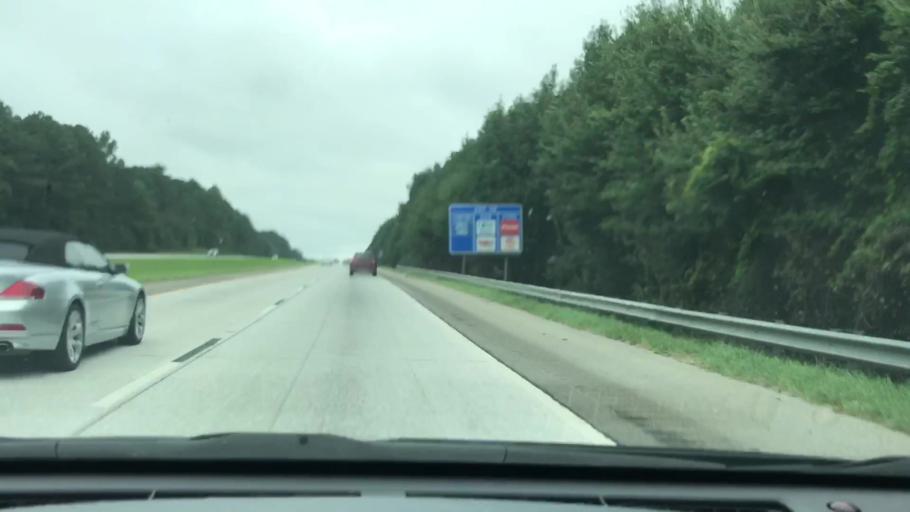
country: US
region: Georgia
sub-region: Morgan County
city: Madison
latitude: 33.5556
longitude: -83.4403
